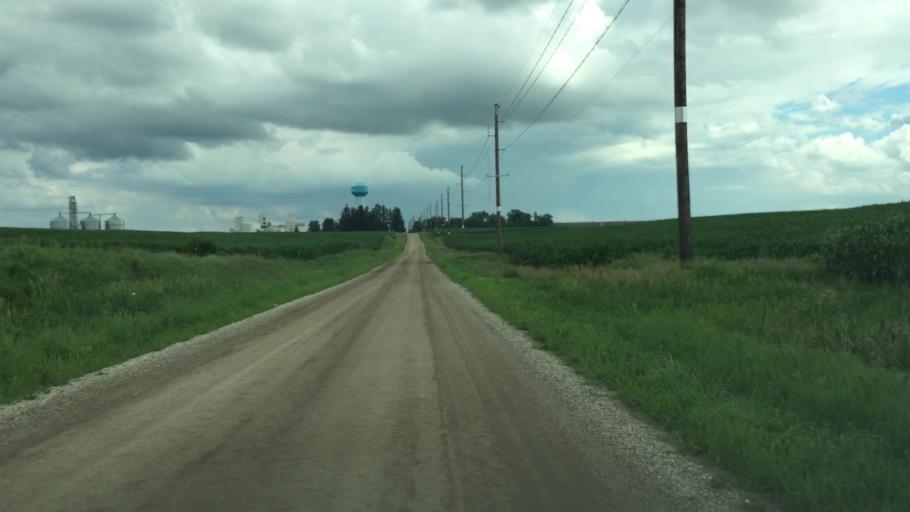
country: US
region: Iowa
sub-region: Jasper County
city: Newton
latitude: 41.7430
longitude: -93.0195
